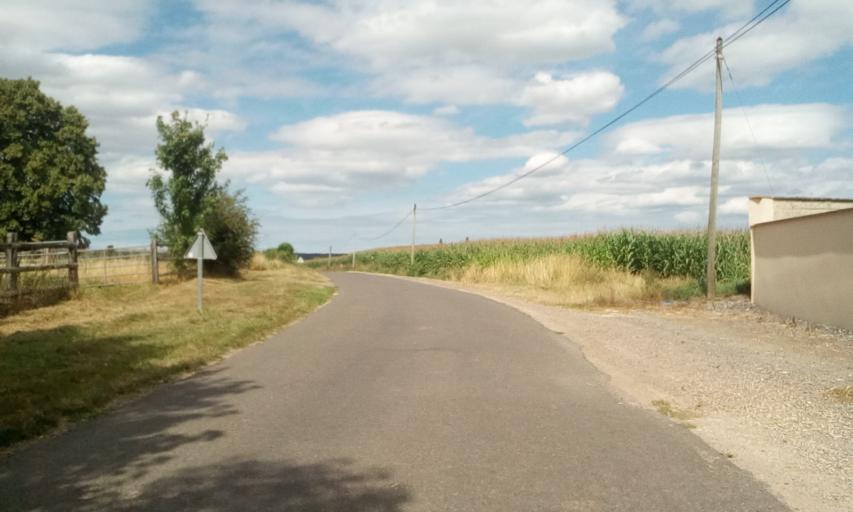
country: FR
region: Lower Normandy
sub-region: Departement du Calvados
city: Sannerville
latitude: 49.1638
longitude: -0.2138
